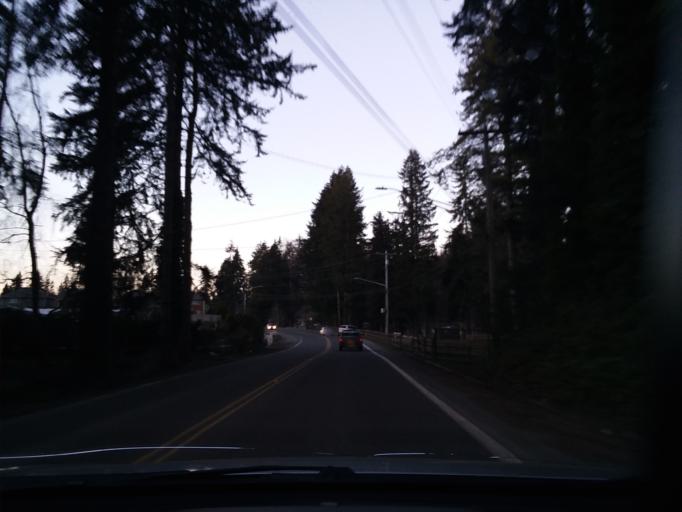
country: US
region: Washington
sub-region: Snohomish County
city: Martha Lake
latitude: 47.8748
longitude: -122.2621
